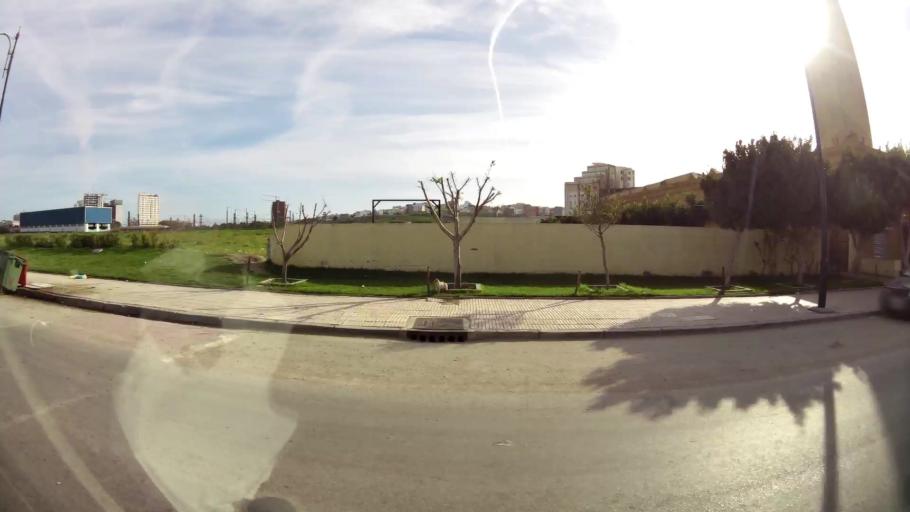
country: MA
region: Tanger-Tetouan
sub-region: Tanger-Assilah
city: Tangier
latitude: 35.7647
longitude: -5.7834
